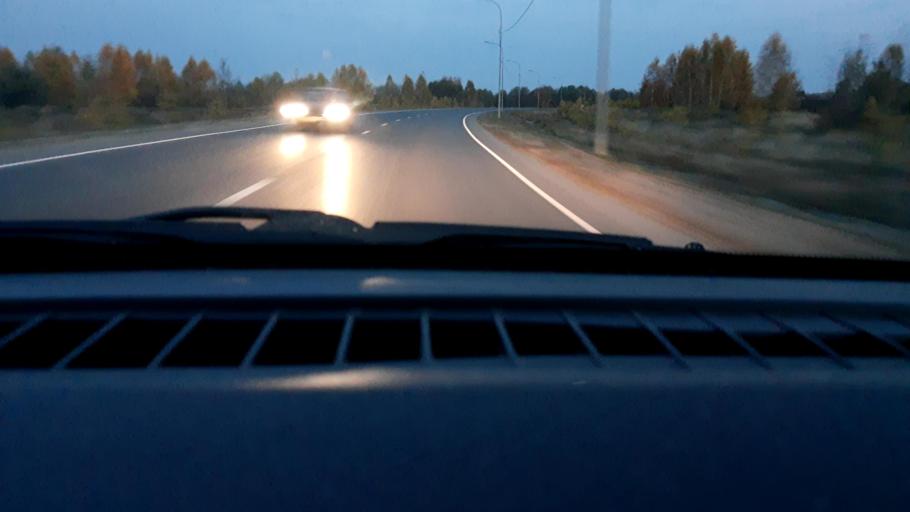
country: RU
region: Nizjnij Novgorod
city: Nizhniy Novgorod
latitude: 56.3758
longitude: 44.0138
